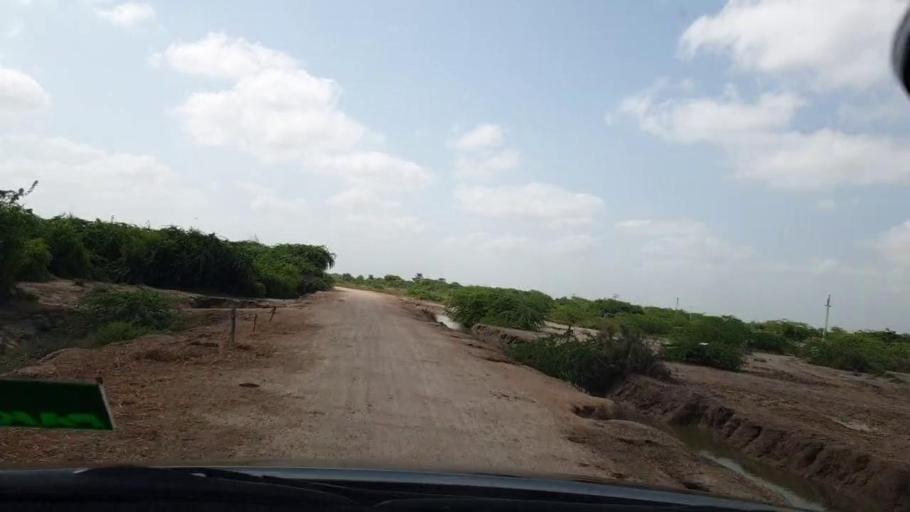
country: PK
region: Sindh
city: Kadhan
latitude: 24.5795
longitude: 69.1517
